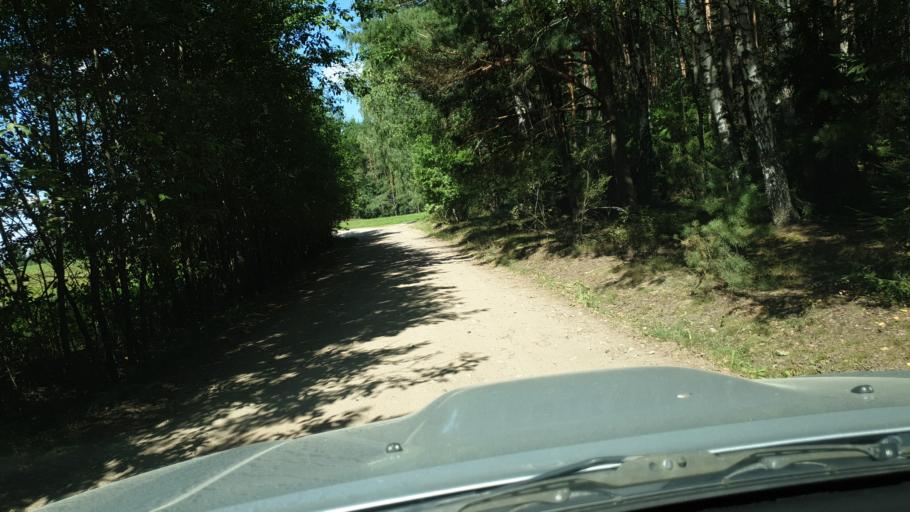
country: LT
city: Sirvintos
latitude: 54.9141
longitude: 24.9251
